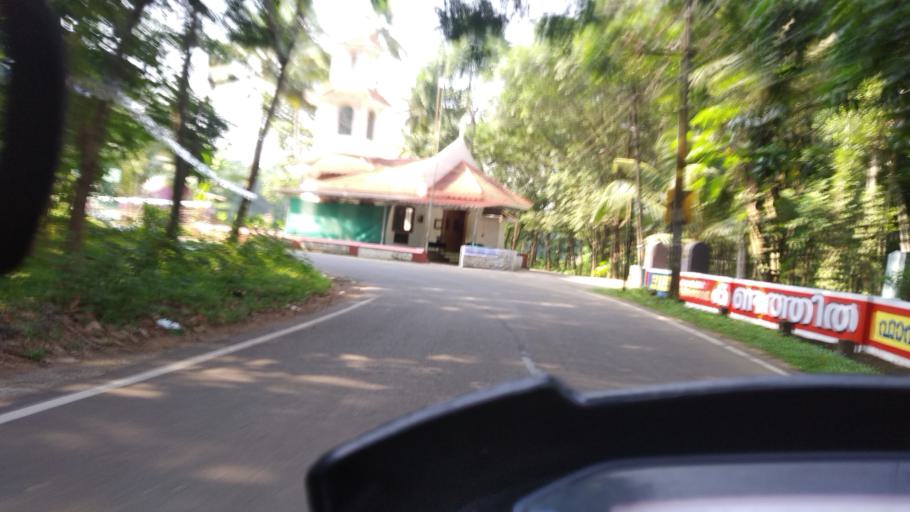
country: IN
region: Kerala
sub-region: Ernakulam
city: Piravam
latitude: 9.8577
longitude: 76.5201
